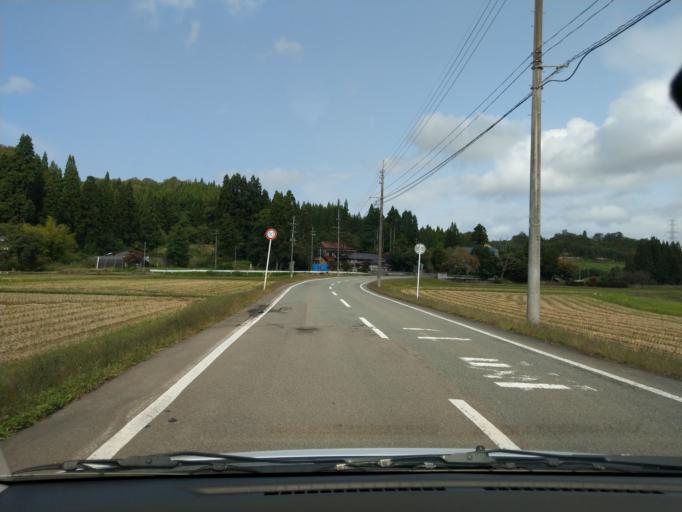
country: JP
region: Akita
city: Omagari
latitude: 39.5049
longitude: 140.3123
